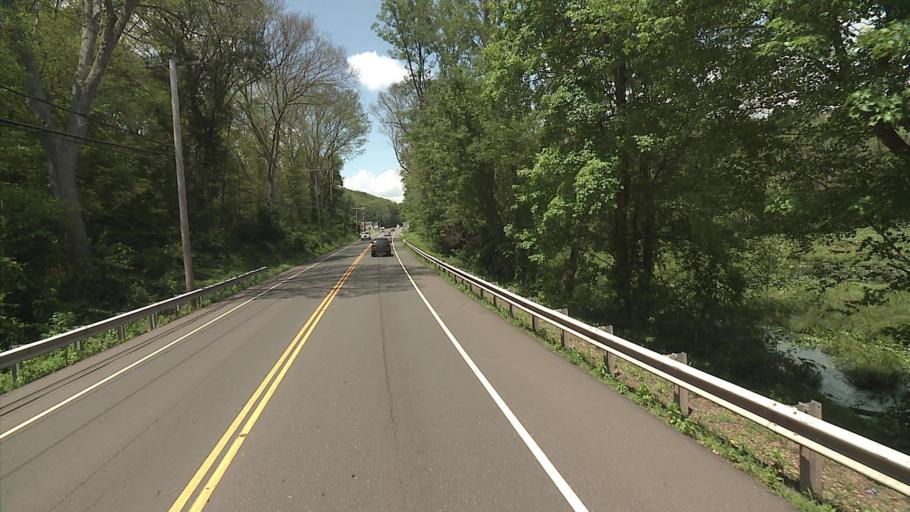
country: US
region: Connecticut
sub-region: Middlesex County
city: East Haddam
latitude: 41.4446
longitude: -72.4717
